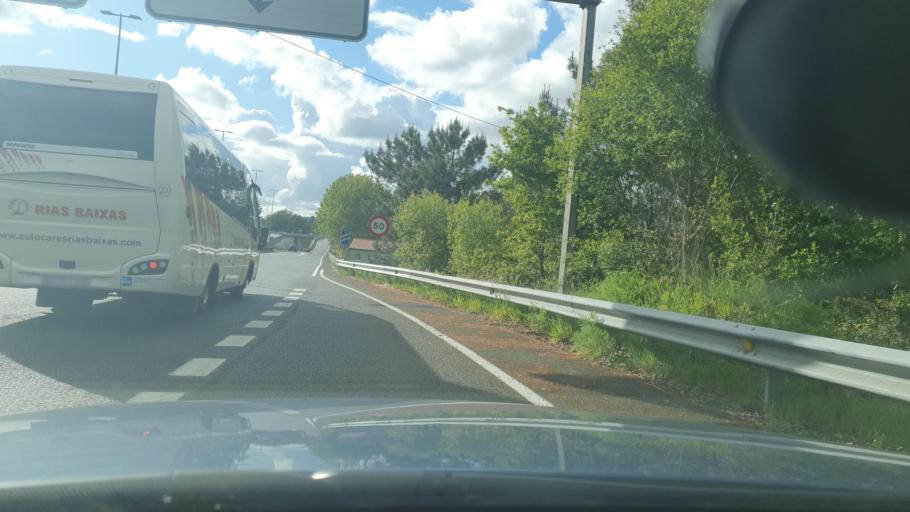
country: ES
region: Galicia
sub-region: Provincia da Coruna
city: Santiago de Compostela
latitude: 42.8680
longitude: -8.5728
